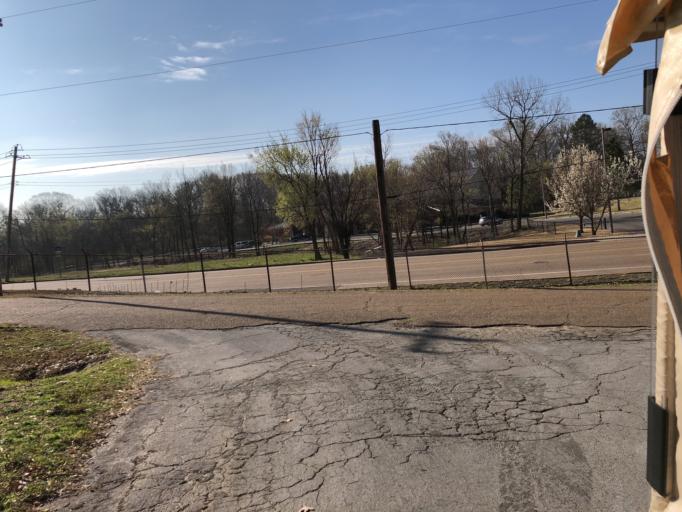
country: US
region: Tennessee
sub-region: Shelby County
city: New South Memphis
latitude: 35.0820
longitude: -89.9928
